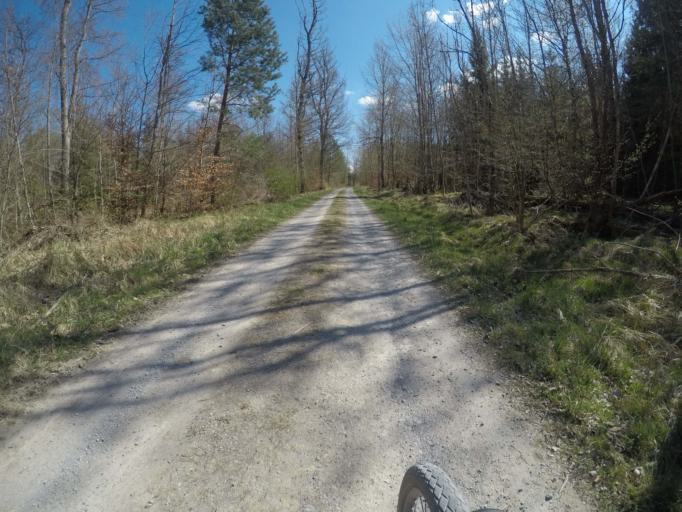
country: DE
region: Baden-Wuerttemberg
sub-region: Regierungsbezirk Stuttgart
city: Altdorf
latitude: 48.6095
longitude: 9.0145
